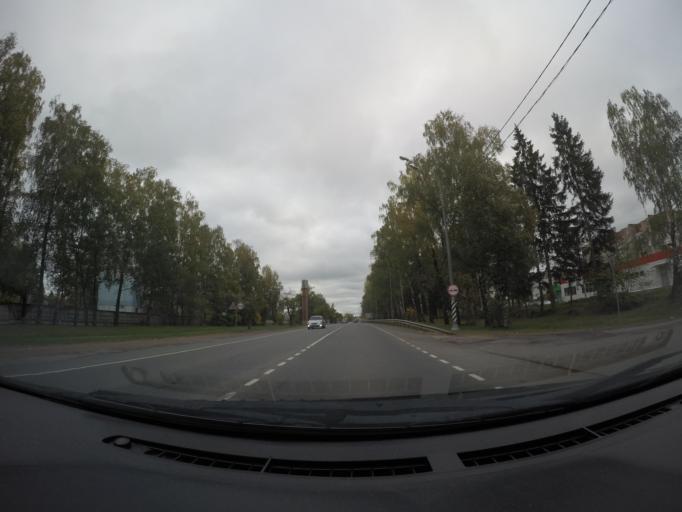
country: RU
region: Moskovskaya
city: Dorokhovo
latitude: 55.6290
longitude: 36.3372
